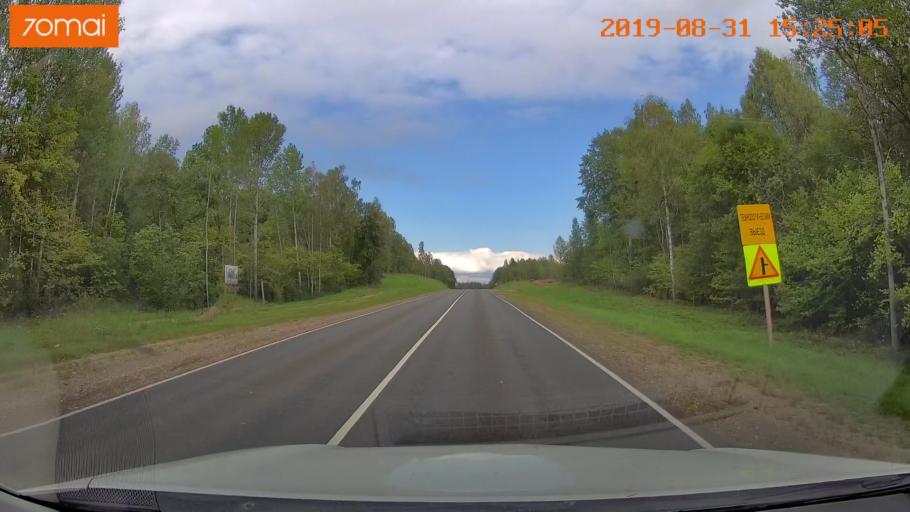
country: RU
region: Kaluga
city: Baryatino
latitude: 54.5364
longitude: 34.5142
